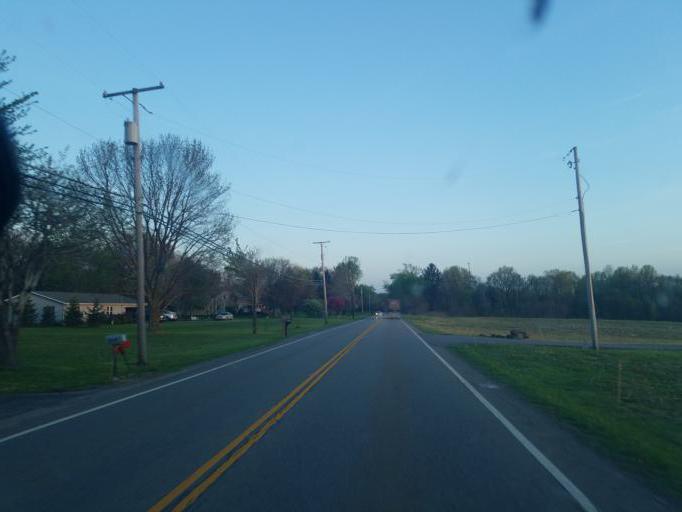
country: US
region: Ohio
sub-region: Trumbull County
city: Brookfield Center
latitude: 41.2172
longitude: -80.5680
